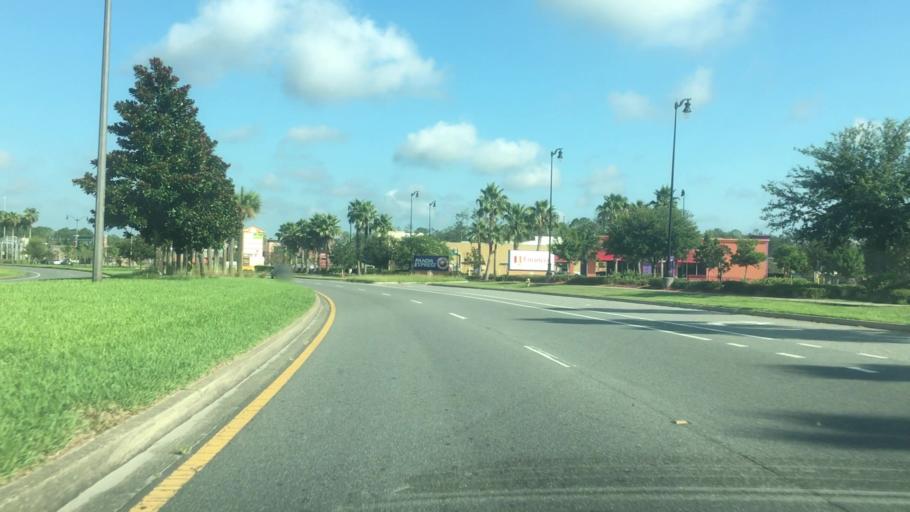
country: US
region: Florida
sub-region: Duval County
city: Jacksonville
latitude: 30.4803
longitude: -81.6365
